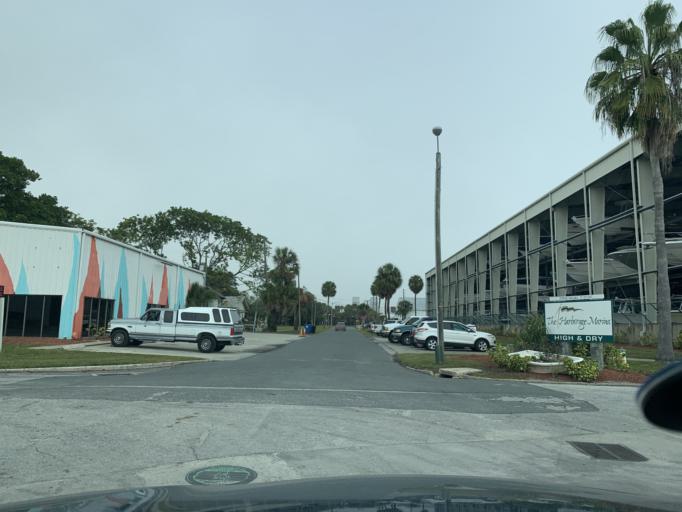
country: US
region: Florida
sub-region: Pinellas County
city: Saint Petersburg
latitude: 27.7558
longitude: -82.6354
